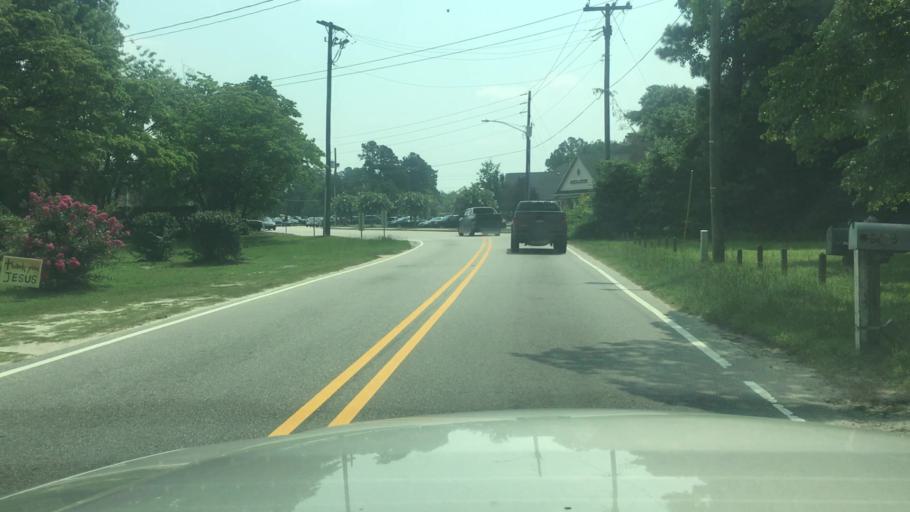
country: US
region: North Carolina
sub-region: Cumberland County
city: Fayetteville
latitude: 35.0363
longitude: -78.9405
